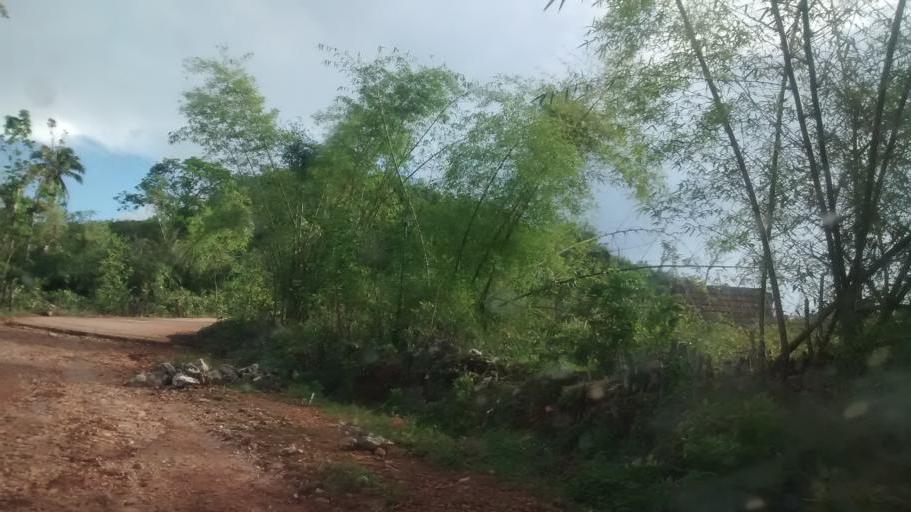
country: HT
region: Grandans
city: Corail
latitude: 18.5146
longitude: -73.7850
